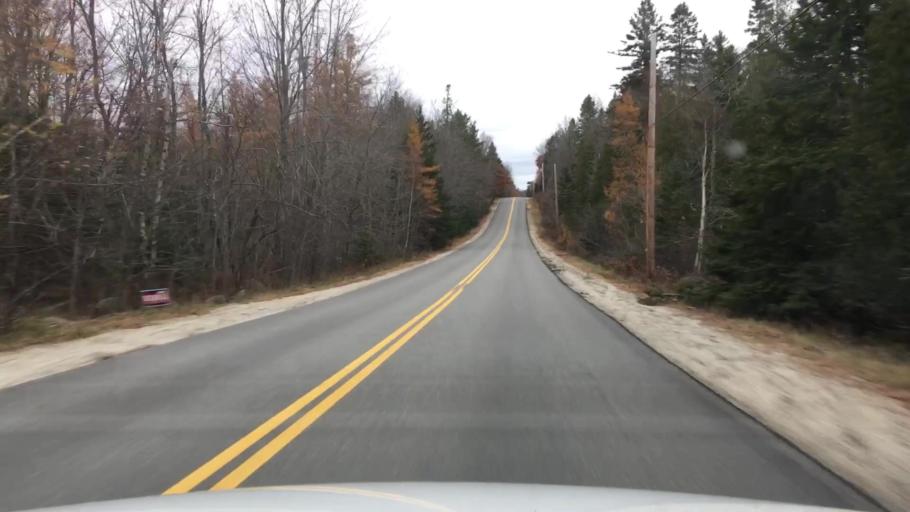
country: US
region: Maine
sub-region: Hancock County
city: Penobscot
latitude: 44.4502
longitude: -68.6370
